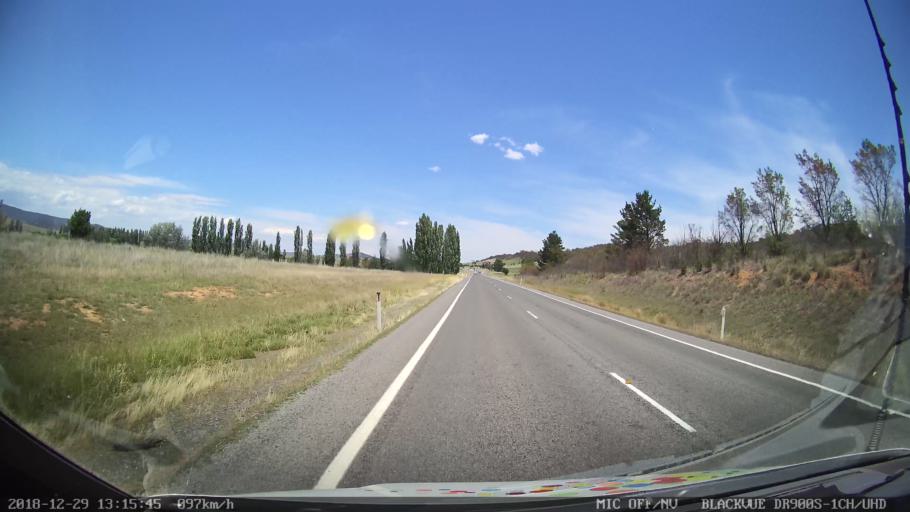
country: AU
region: Australian Capital Territory
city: Macarthur
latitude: -35.7135
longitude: 149.1587
